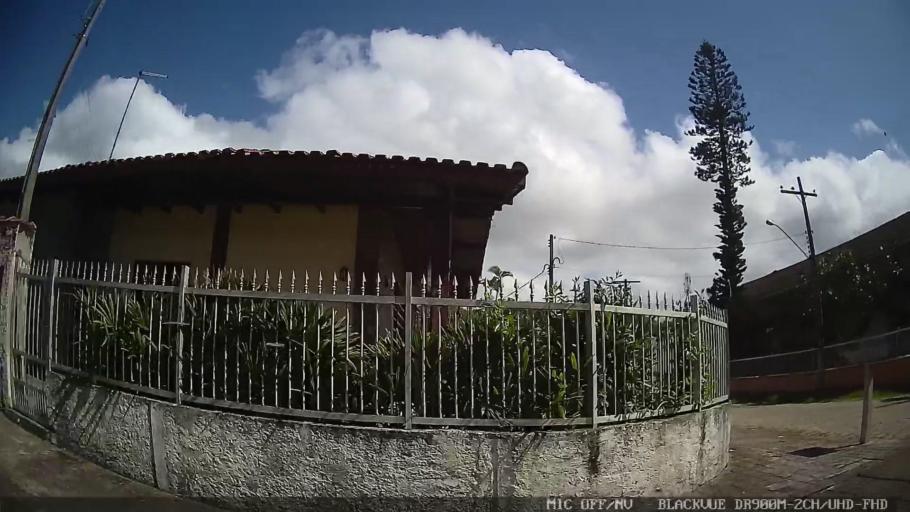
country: BR
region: Sao Paulo
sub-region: Peruibe
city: Peruibe
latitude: -24.3210
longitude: -46.9930
